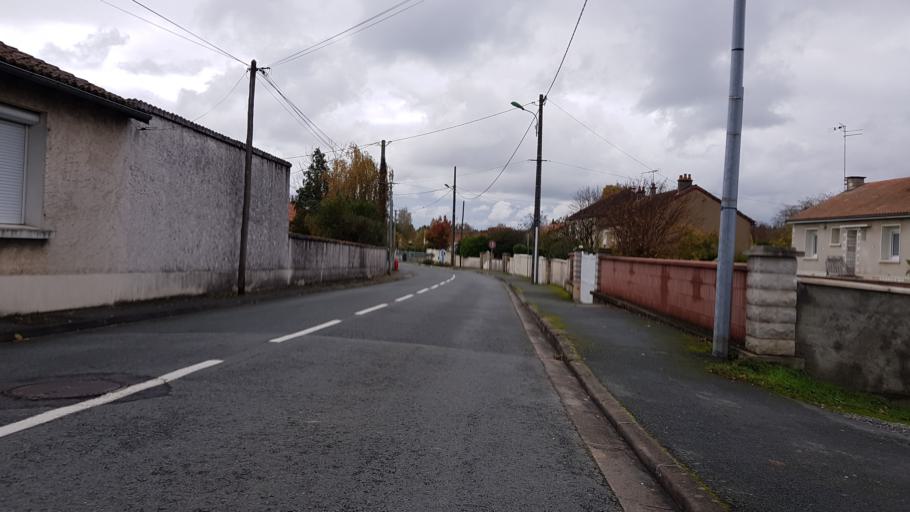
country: FR
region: Poitou-Charentes
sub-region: Departement de la Vienne
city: Chasseneuil-du-Poitou
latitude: 46.6439
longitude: 0.3647
